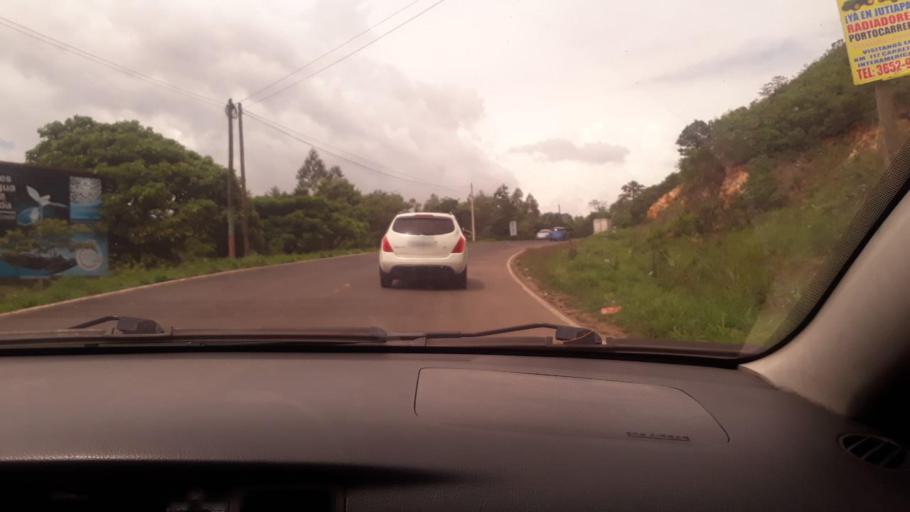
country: GT
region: Jutiapa
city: Quesada
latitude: 14.2768
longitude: -89.9930
